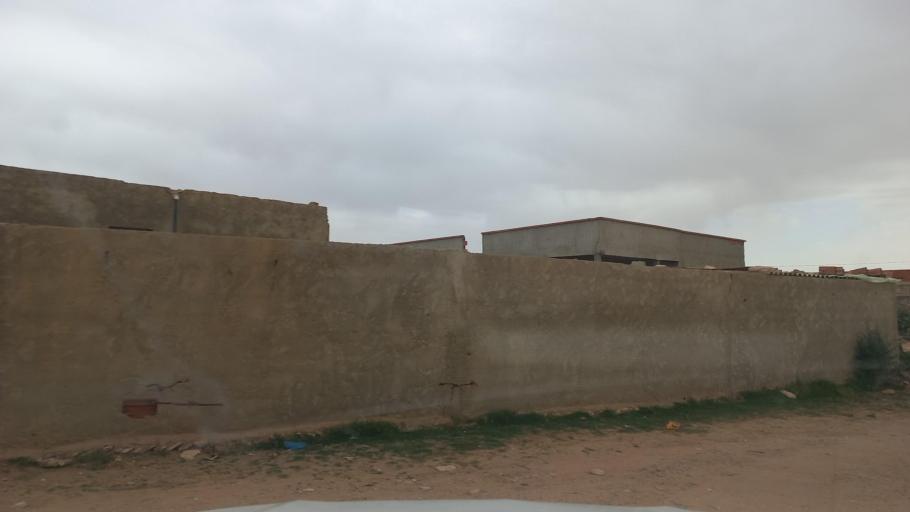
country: TN
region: Al Qasrayn
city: Sbiba
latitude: 35.3834
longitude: 9.0629
